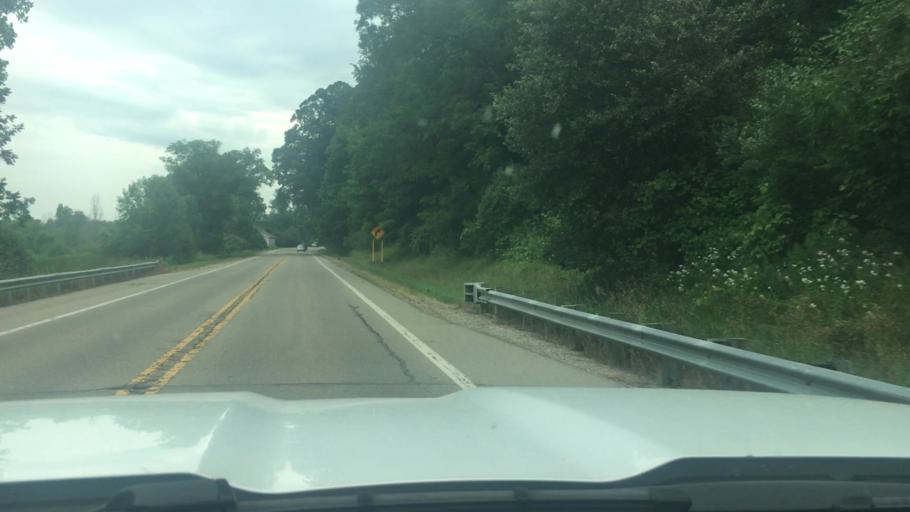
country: US
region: Michigan
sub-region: Ionia County
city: Saranac
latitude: 42.9591
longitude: -85.1632
